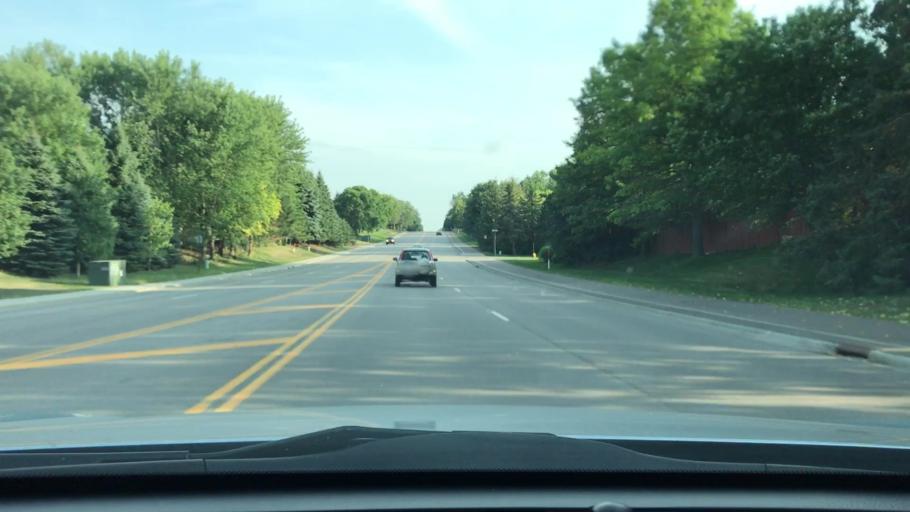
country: US
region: Minnesota
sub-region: Hennepin County
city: Maple Grove
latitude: 45.0420
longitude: -93.4818
